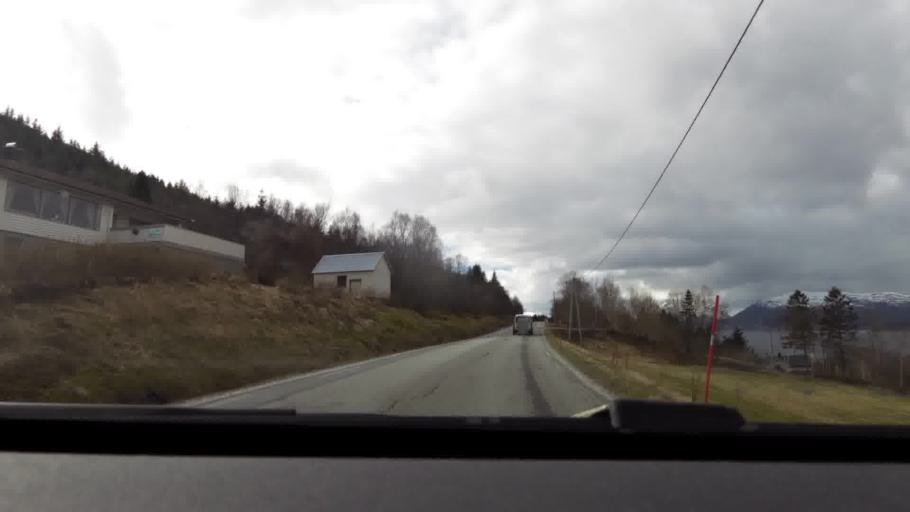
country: NO
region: More og Romsdal
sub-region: Gjemnes
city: Batnfjordsora
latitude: 62.9414
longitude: 7.6140
